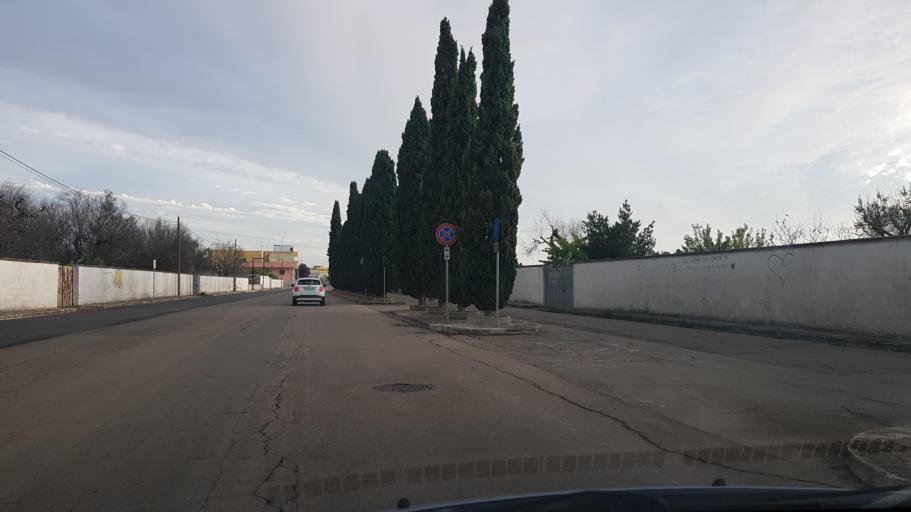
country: IT
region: Apulia
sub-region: Provincia di Lecce
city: Surbo
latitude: 40.4035
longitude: 18.1280
